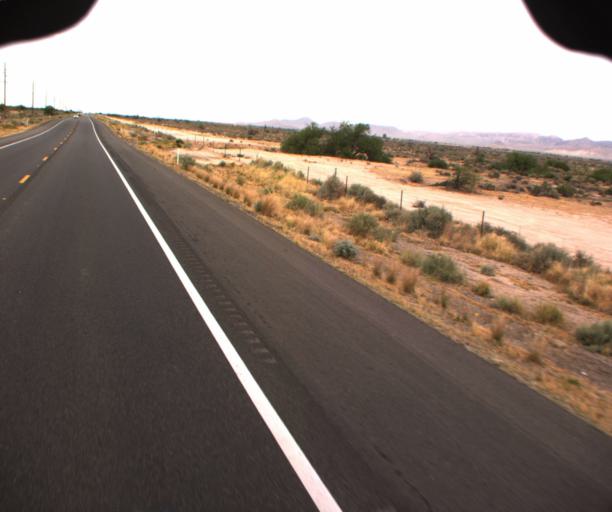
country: US
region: Arizona
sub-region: Pinal County
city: Blackwater
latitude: 33.0365
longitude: -111.6559
